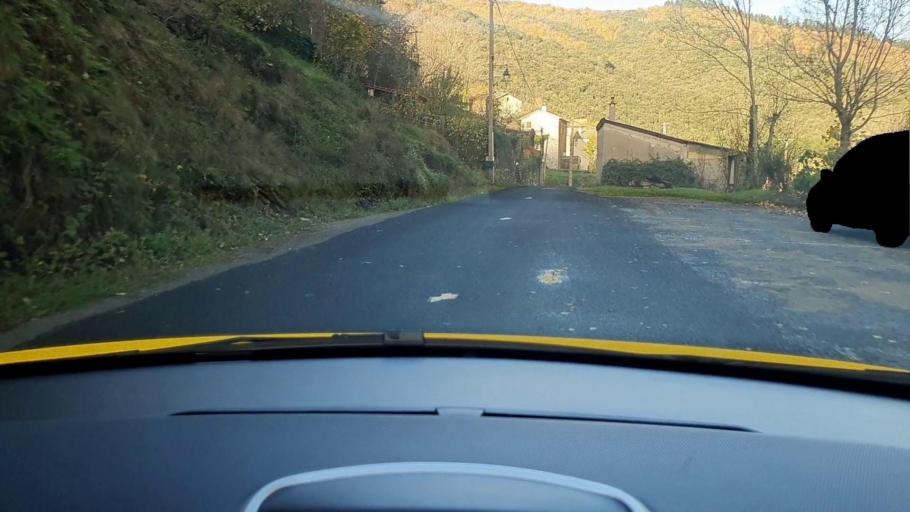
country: FR
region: Languedoc-Roussillon
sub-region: Departement du Gard
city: Valleraugue
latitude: 44.1071
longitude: 3.7253
